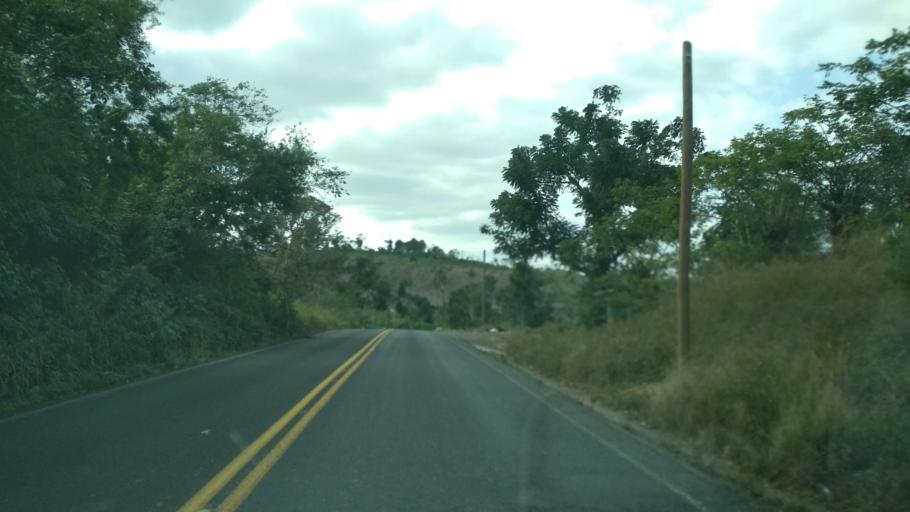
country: MX
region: Veracruz
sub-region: Papantla
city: Polutla
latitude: 20.4671
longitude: -97.2585
